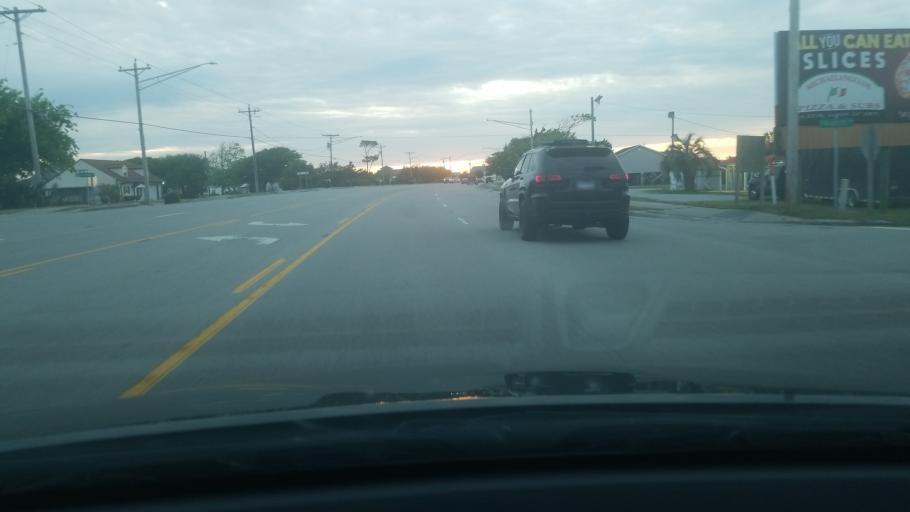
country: US
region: North Carolina
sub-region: Onslow County
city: Swansboro
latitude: 34.6768
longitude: -77.1038
